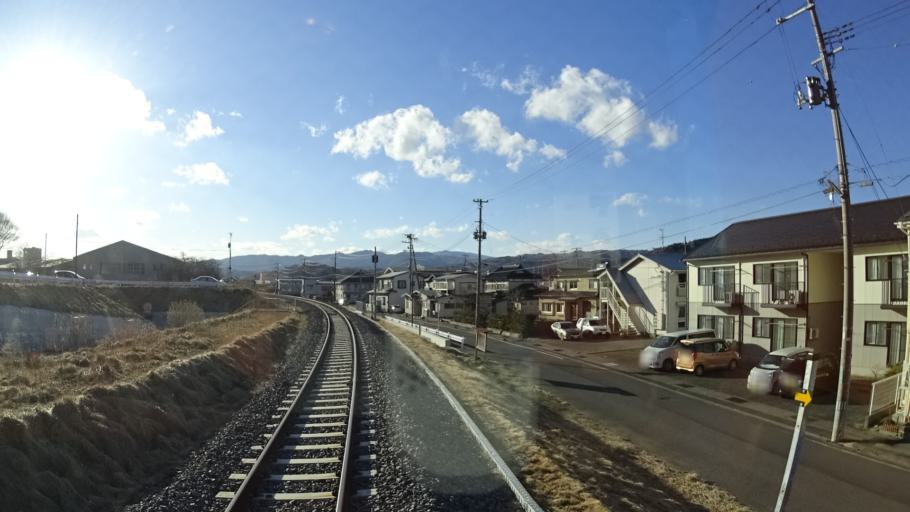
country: JP
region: Iwate
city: Miyako
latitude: 39.6369
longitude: 141.9592
